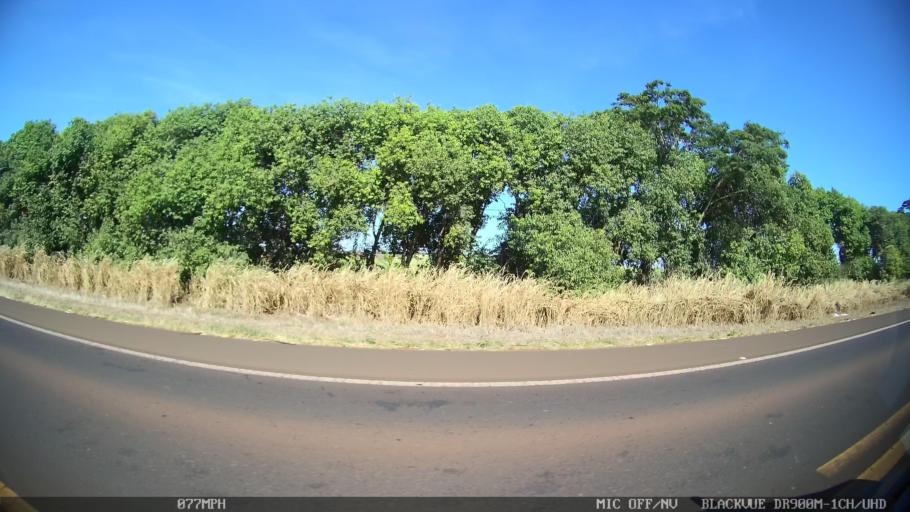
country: BR
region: Sao Paulo
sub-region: Barretos
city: Barretos
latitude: -20.5713
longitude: -48.6718
